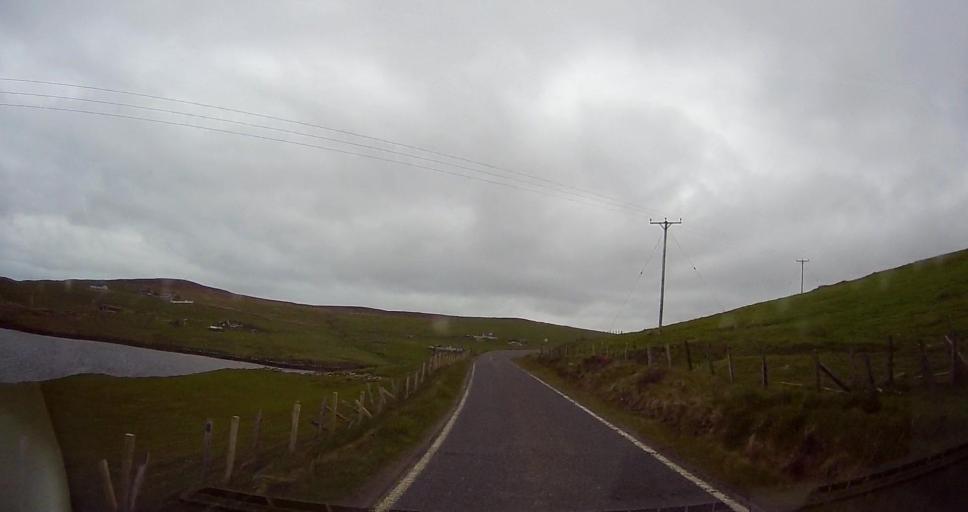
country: GB
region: Scotland
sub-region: Shetland Islands
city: Lerwick
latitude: 60.3006
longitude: -1.3546
